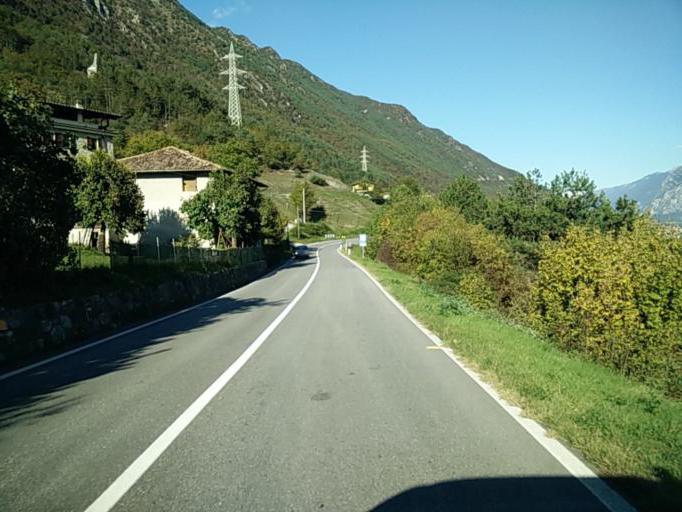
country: IT
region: Lombardy
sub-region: Provincia di Brescia
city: Ponte Caffaro
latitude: 45.8026
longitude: 10.5055
